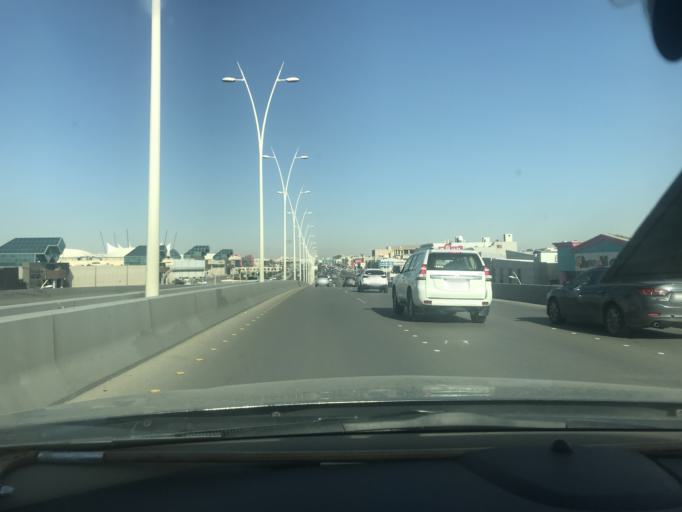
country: SA
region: Ar Riyad
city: Riyadh
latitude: 24.7374
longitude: 46.6850
